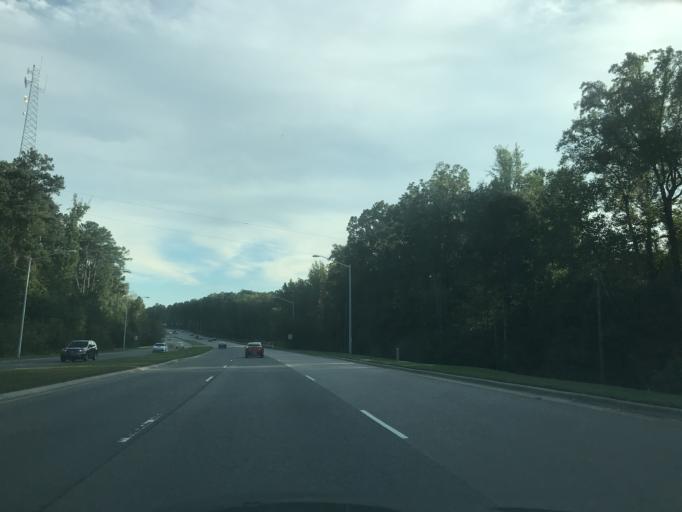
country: US
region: North Carolina
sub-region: Wake County
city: Green Level
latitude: 35.8558
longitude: -78.8948
